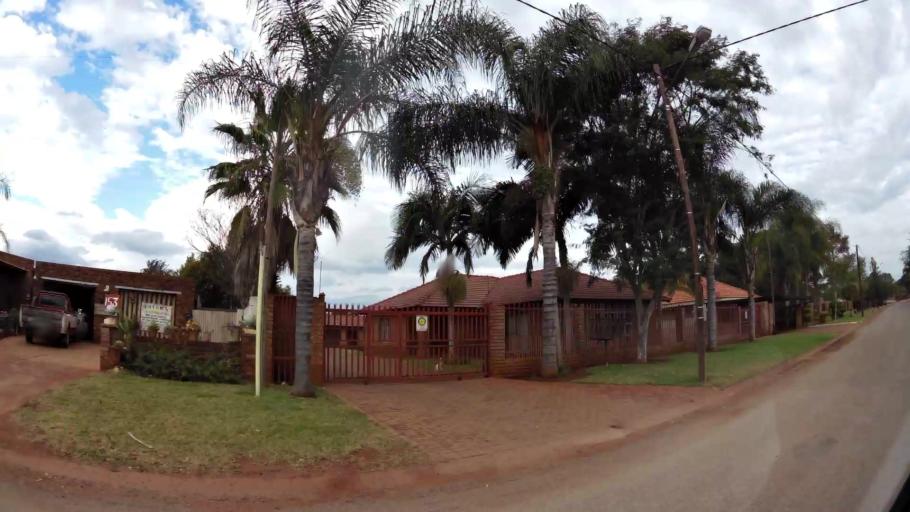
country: ZA
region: Limpopo
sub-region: Waterberg District Municipality
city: Modimolle
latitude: -24.5063
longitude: 28.7237
